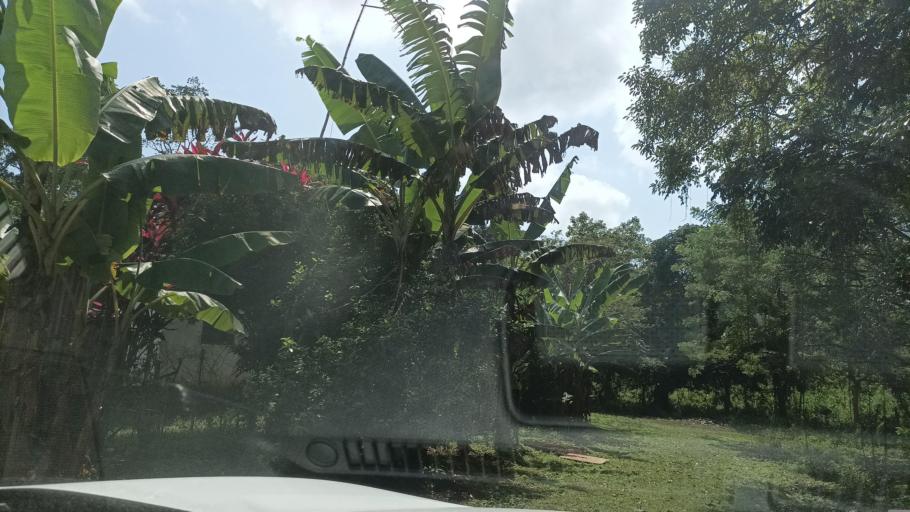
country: MX
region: Veracruz
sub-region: Pajapan
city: Pajapan
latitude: 18.1816
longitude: -94.6724
